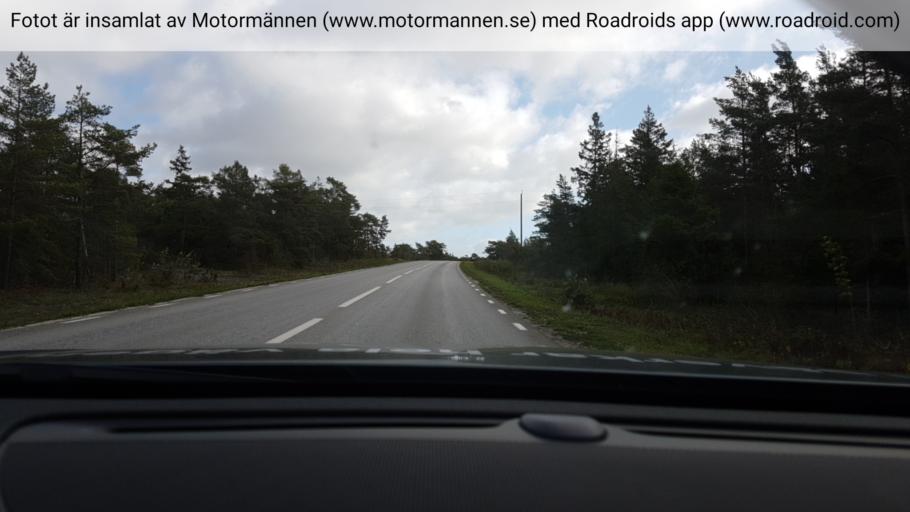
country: SE
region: Gotland
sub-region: Gotland
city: Slite
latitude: 57.8560
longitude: 18.9968
